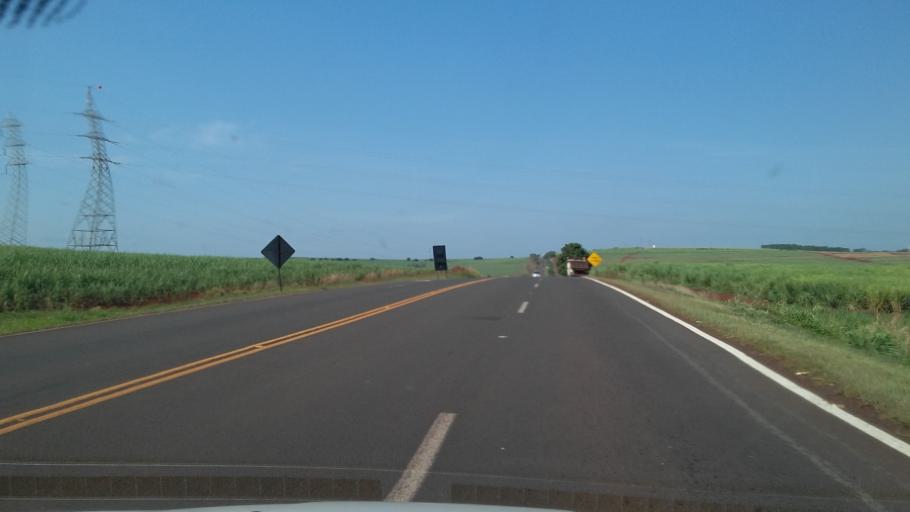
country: BR
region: Parana
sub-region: Bandeirantes
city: Bandeirantes
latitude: -23.1144
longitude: -50.3398
